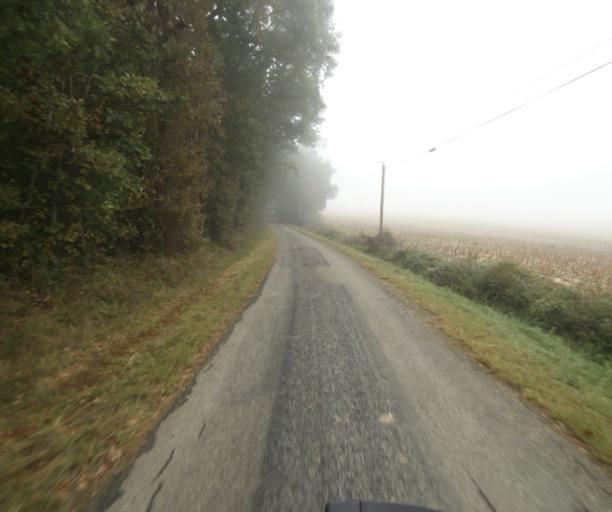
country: FR
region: Midi-Pyrenees
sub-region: Departement du Tarn-et-Garonne
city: Nohic
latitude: 43.9080
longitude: 1.4738
